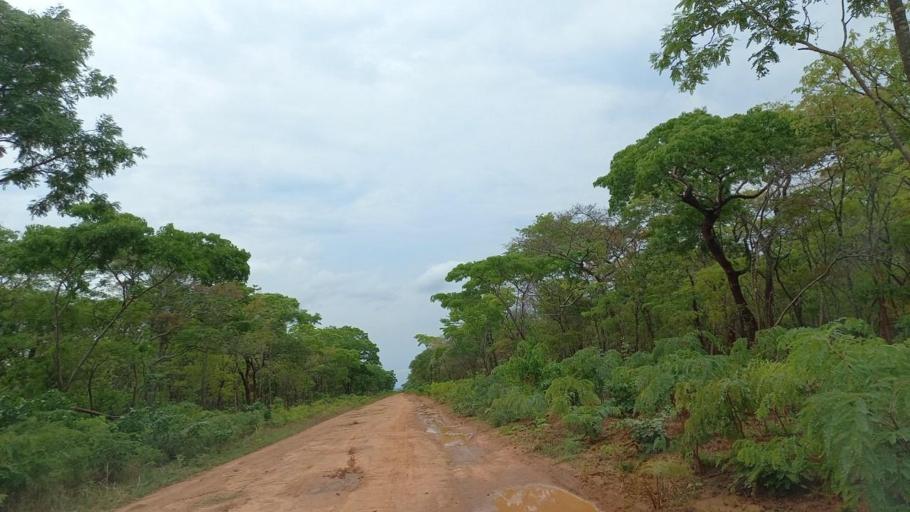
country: ZM
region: North-Western
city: Kalengwa
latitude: -13.6129
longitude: 24.9757
